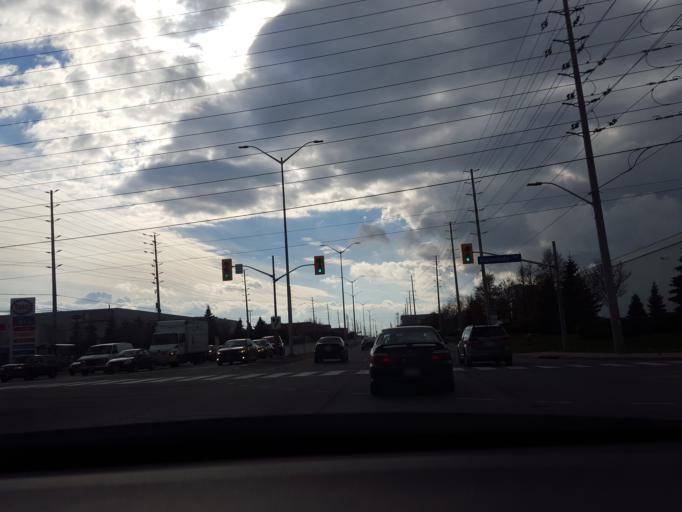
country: CA
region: Ontario
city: Brampton
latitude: 43.6560
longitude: -79.6954
